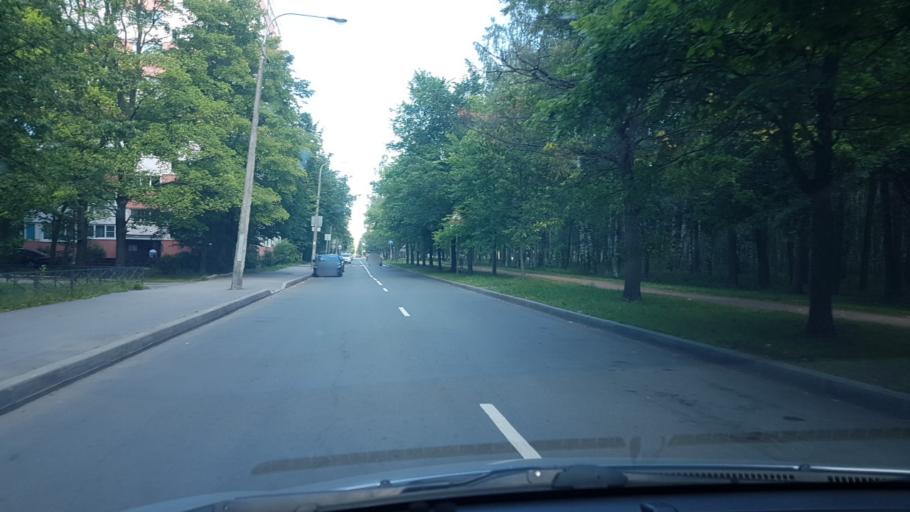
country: RU
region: St.-Petersburg
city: Dachnoye
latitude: 59.8321
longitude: 30.2256
